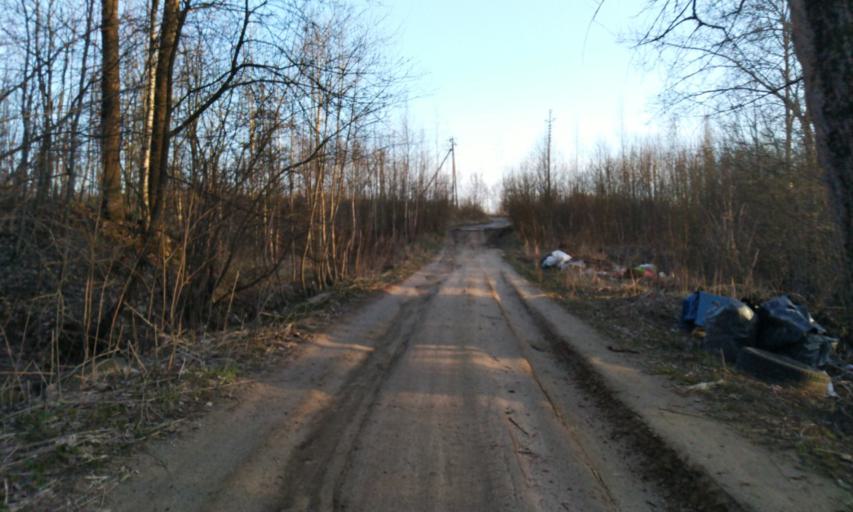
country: RU
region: Leningrad
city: Novoye Devyatkino
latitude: 60.0846
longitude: 30.4593
